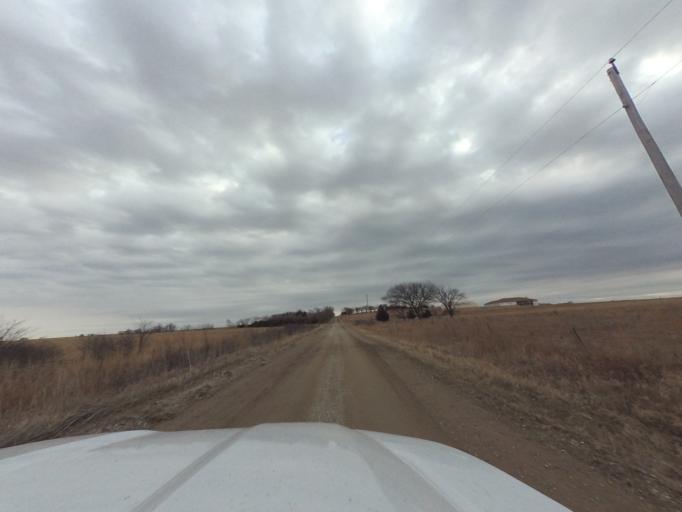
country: US
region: Kansas
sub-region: Chase County
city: Cottonwood Falls
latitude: 38.4492
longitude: -96.3778
